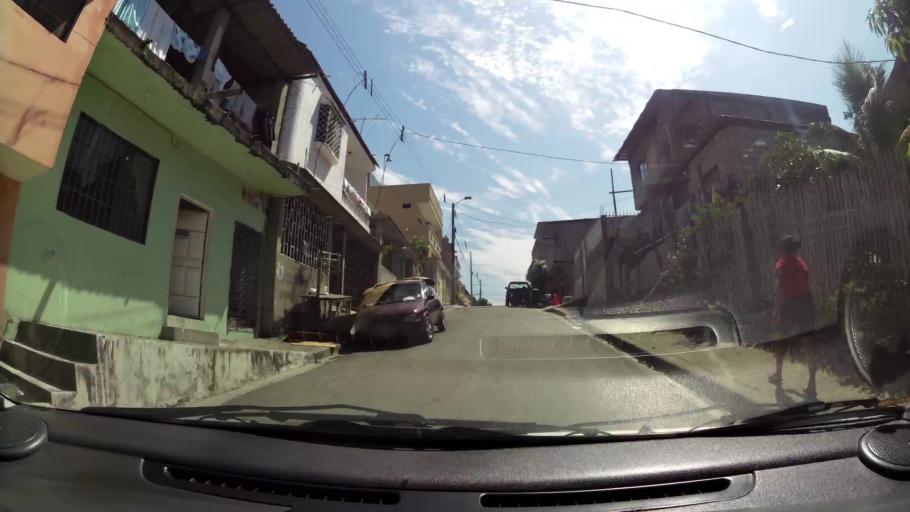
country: EC
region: Guayas
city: Eloy Alfaro
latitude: -2.1295
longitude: -79.9158
